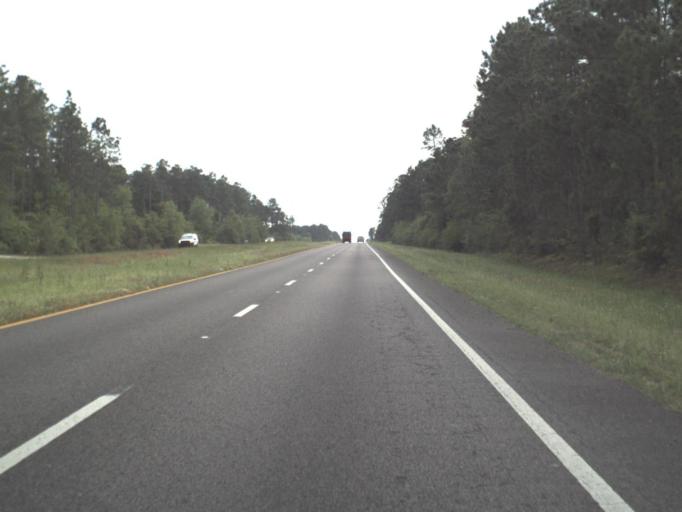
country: US
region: Florida
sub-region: Escambia County
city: Molino
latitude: 30.6891
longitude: -87.3510
